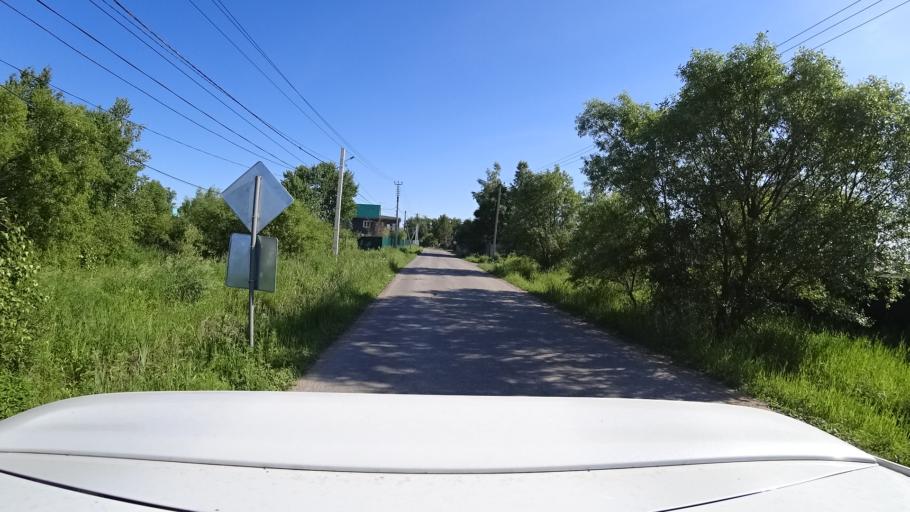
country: RU
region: Khabarovsk Krai
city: Topolevo
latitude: 48.5446
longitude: 135.1740
